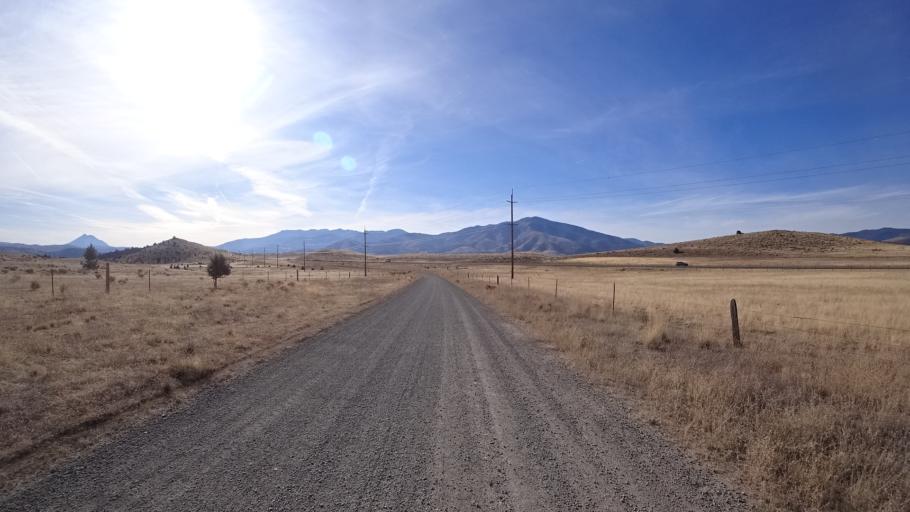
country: US
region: California
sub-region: Siskiyou County
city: Weed
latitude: 41.5268
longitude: -122.4744
